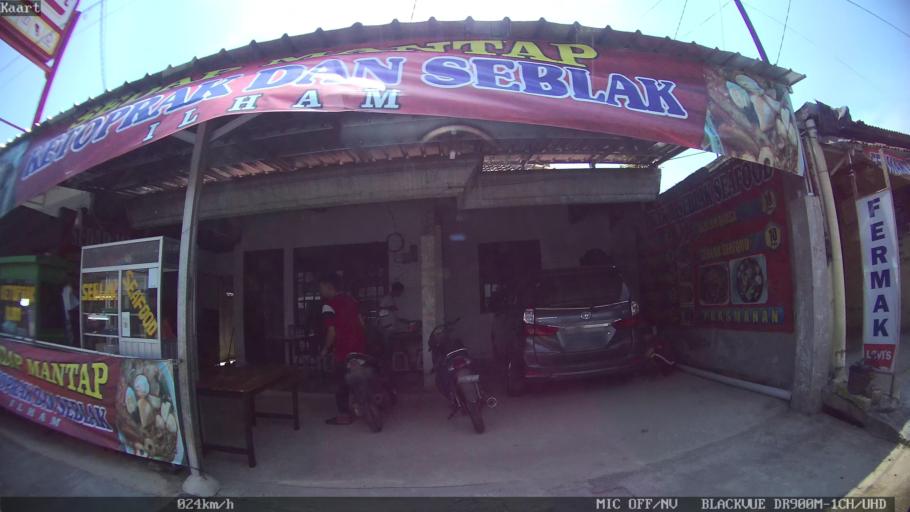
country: ID
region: Lampung
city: Kedaton
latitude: -5.3980
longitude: 105.2647
